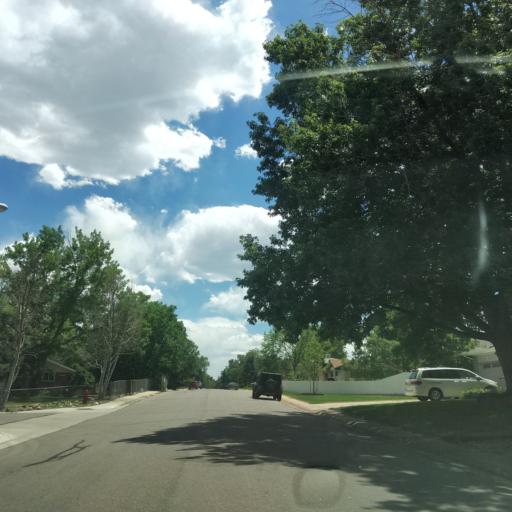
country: US
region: Colorado
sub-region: Jefferson County
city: Lakewood
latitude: 39.6888
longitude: -105.0957
